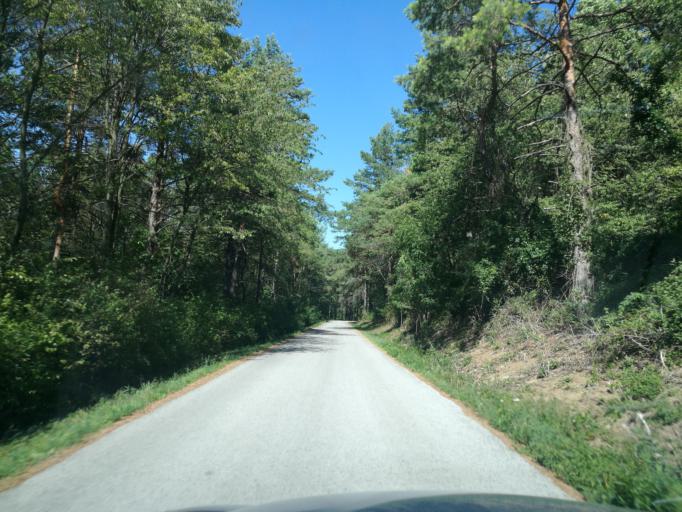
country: SK
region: Nitriansky
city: Brezova pod Bradlom
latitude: 48.6791
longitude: 17.5467
